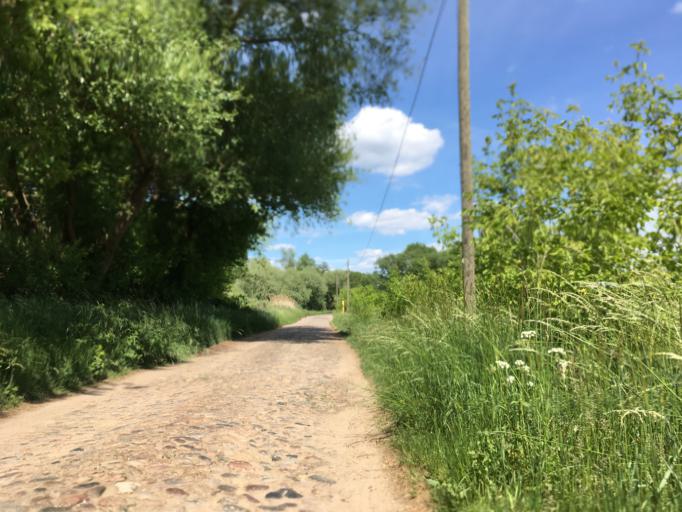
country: DE
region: Brandenburg
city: Oderberg
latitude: 52.8641
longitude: 14.0766
